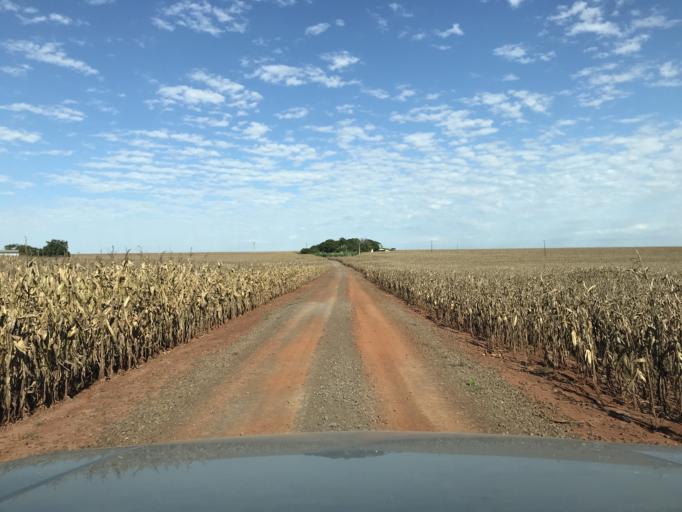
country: BR
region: Parana
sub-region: Palotina
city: Palotina
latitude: -24.1712
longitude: -53.7586
